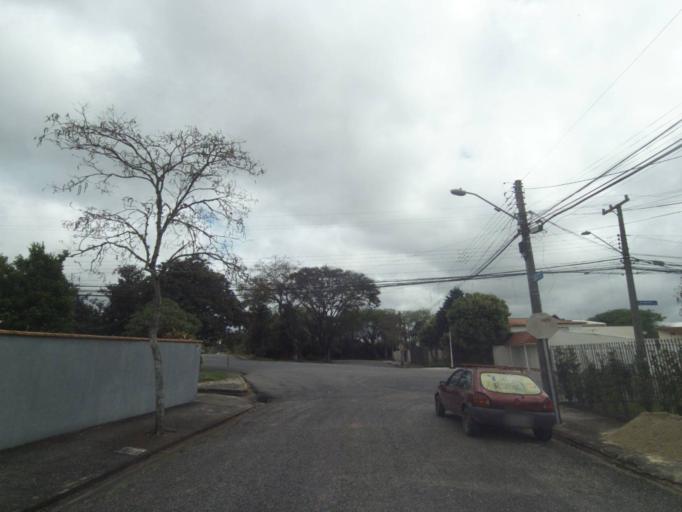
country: BR
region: Parana
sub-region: Pinhais
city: Pinhais
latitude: -25.3965
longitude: -49.2236
